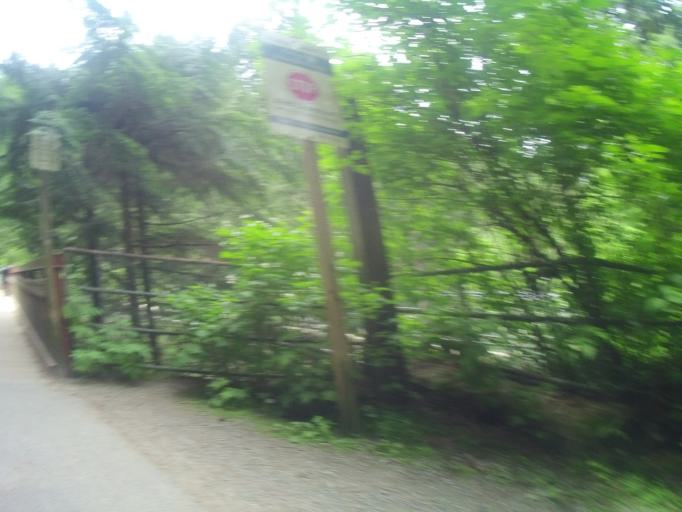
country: CA
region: British Columbia
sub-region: Fraser Valley Regional District
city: North Vancouver
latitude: 49.3497
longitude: -123.0195
